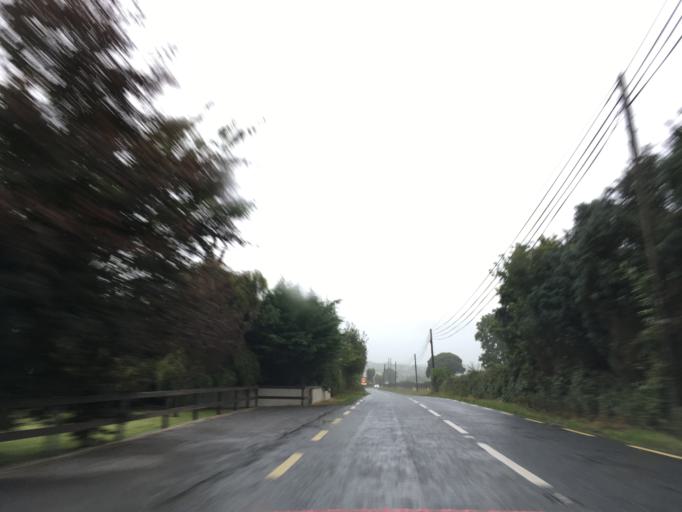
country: IE
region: Munster
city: Tipperary
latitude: 52.4832
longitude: -8.0807
